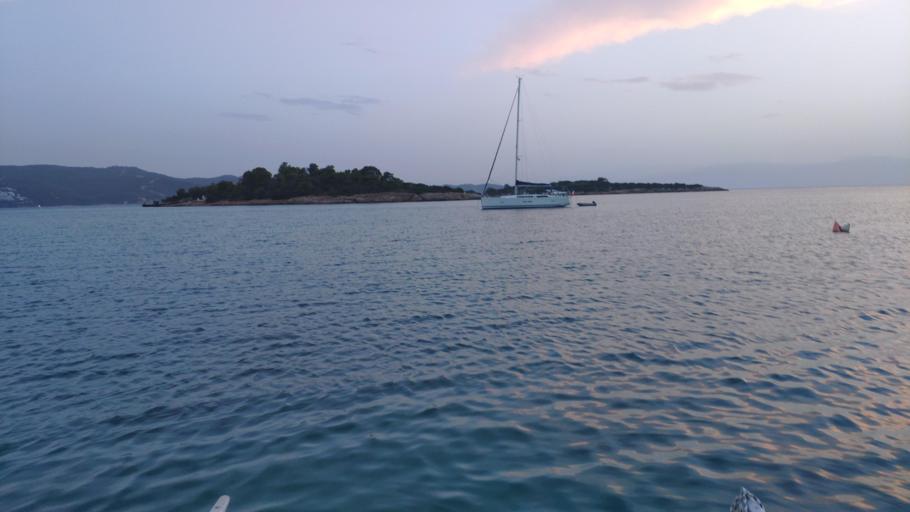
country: GR
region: Peloponnese
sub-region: Nomos Argolidos
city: Porto Cheli
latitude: 37.3054
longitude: 23.1436
